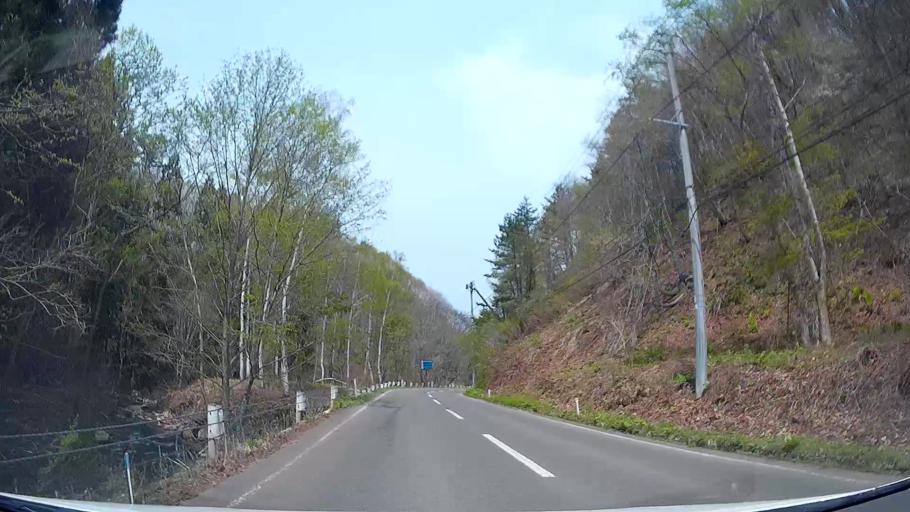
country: JP
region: Akita
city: Hanawa
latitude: 40.0303
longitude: 140.8245
